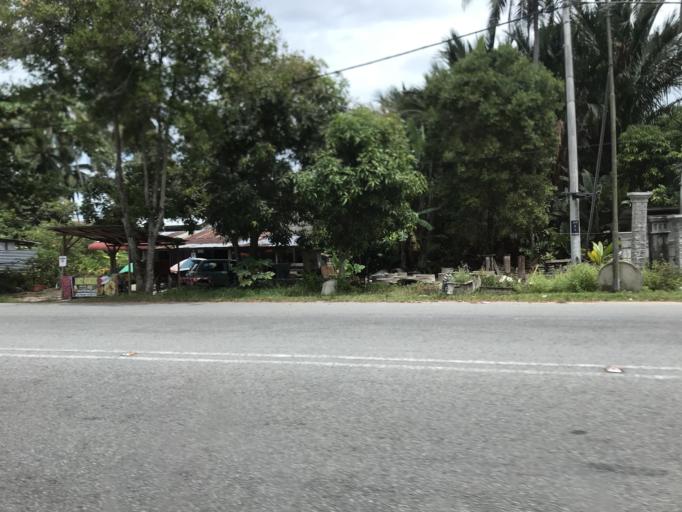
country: MY
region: Kelantan
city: Tumpat
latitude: 6.1765
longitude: 102.1806
